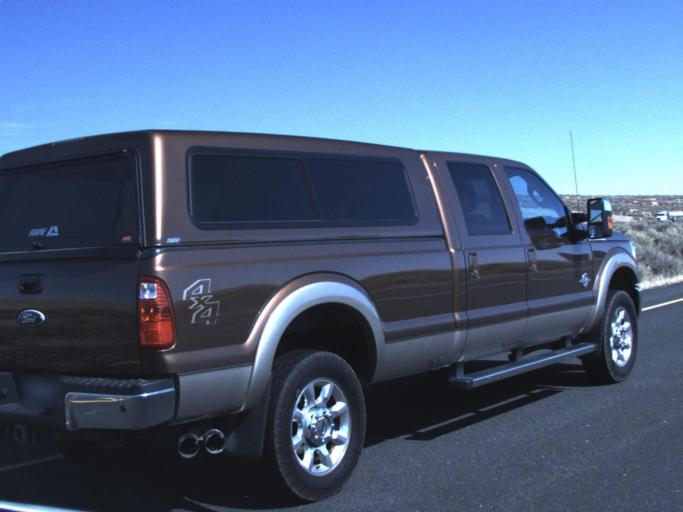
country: US
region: Washington
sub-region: Grant County
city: Warden
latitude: 47.0871
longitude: -118.9016
